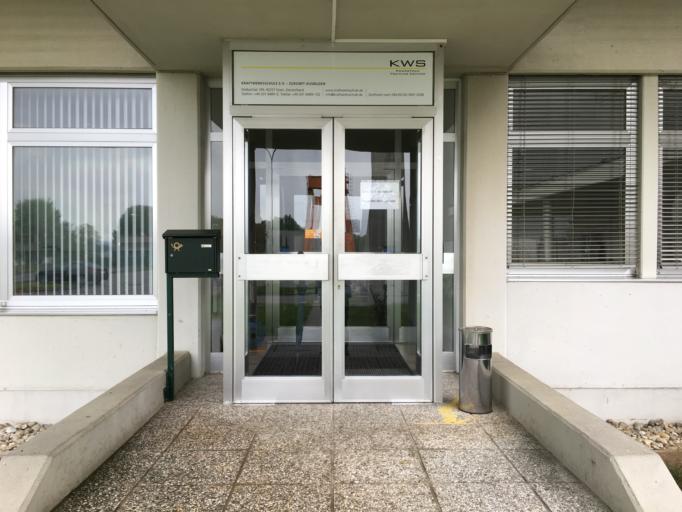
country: AT
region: Lower Austria
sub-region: Politischer Bezirk Tulln
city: Atzenbrugg
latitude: 48.3544
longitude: 15.8866
